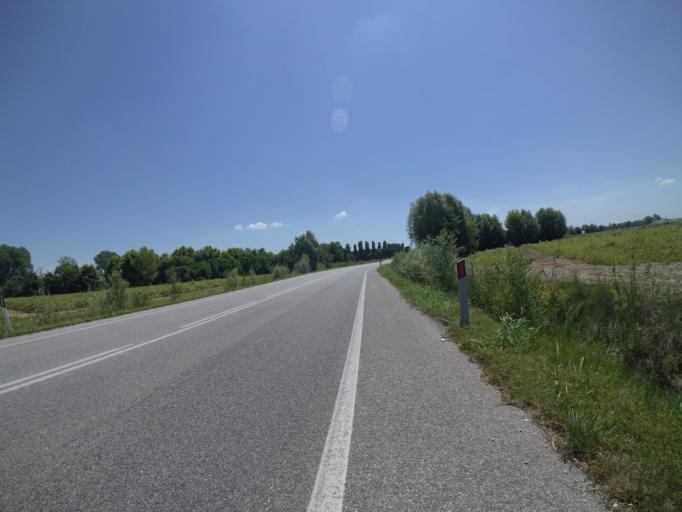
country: IT
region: Friuli Venezia Giulia
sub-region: Provincia di Udine
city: Varmo
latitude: 45.8843
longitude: 13.0104
